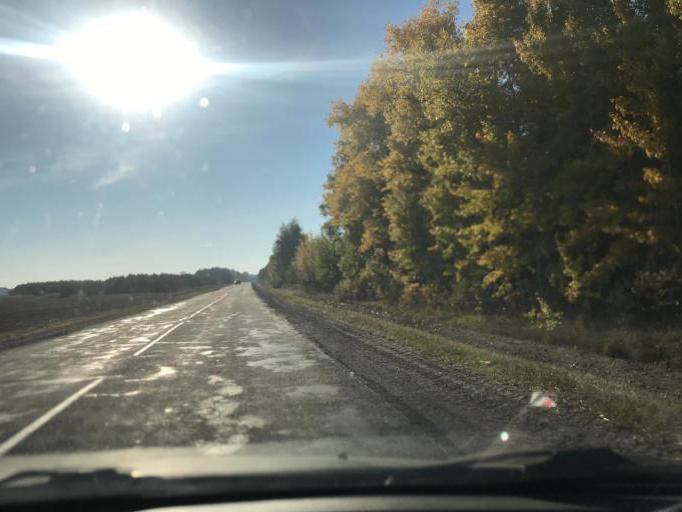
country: BY
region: Gomel
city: Brahin
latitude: 51.7558
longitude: 30.3059
